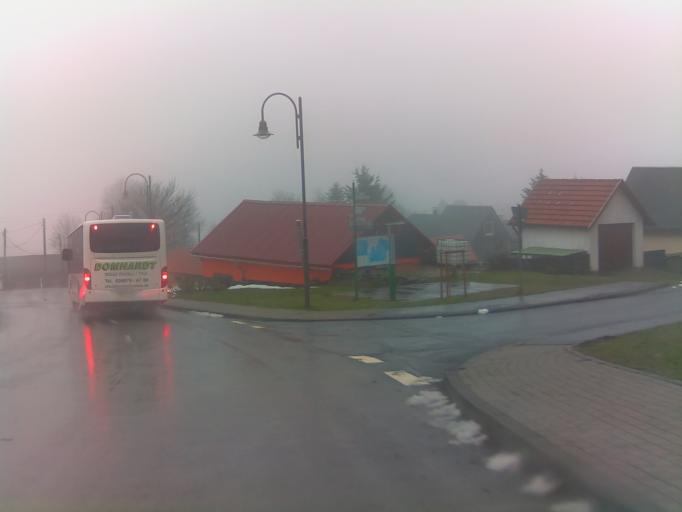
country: DE
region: Thuringia
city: Eisfeld
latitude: 50.4994
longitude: 10.9028
